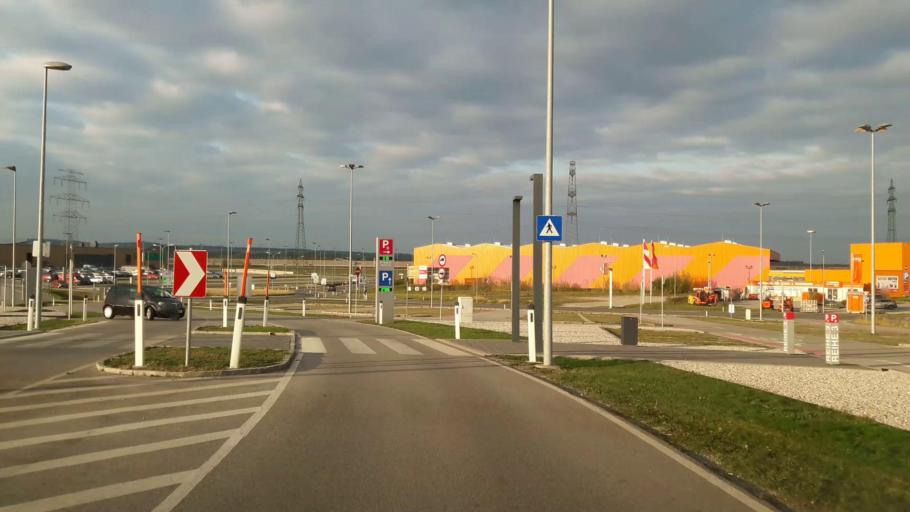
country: AT
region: Lower Austria
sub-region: Politischer Bezirk Mistelbach
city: Grossebersdorf
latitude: 48.3428
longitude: 16.4655
